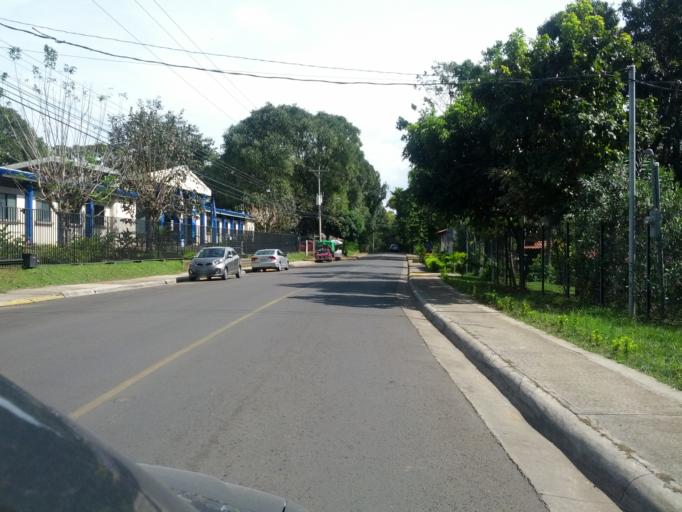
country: CR
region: Heredia
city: Llorente
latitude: 10.0178
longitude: -84.1775
